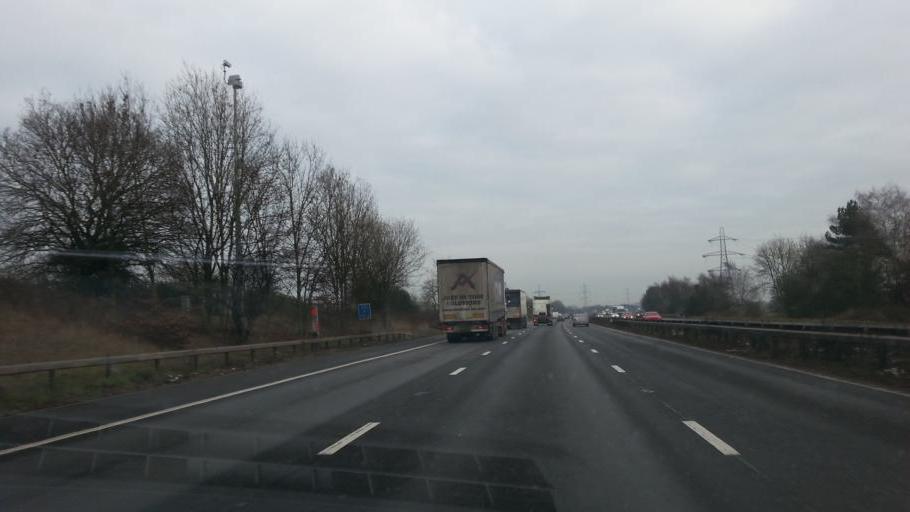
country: GB
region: England
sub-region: Warwickshire
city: Exhall
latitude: 52.4665
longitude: -1.5067
